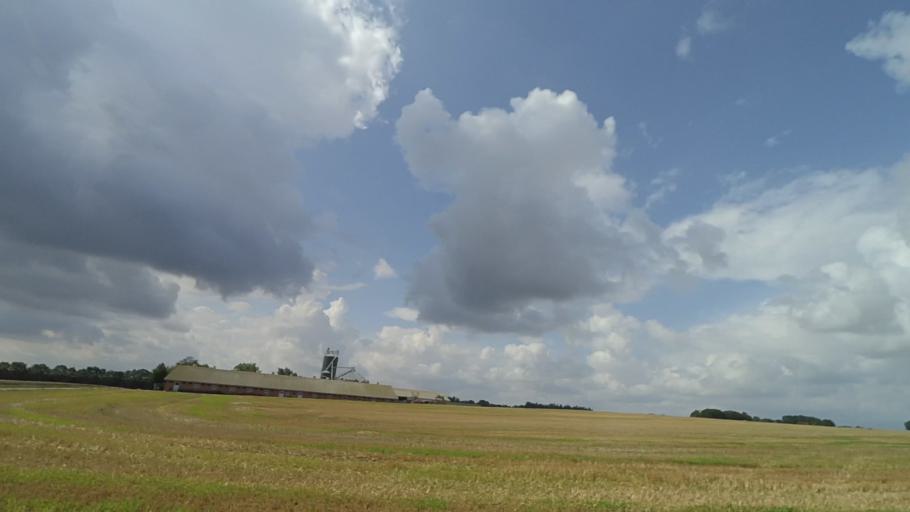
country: DK
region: Central Jutland
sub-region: Norddjurs Kommune
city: Allingabro
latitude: 56.5032
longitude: 10.3752
